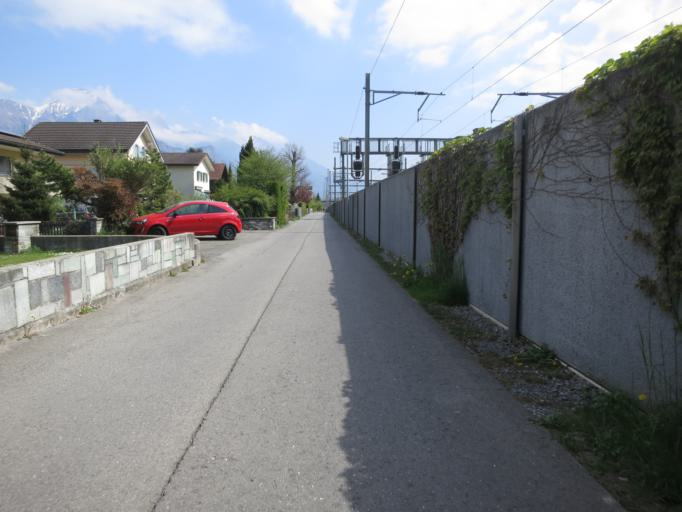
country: CH
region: Saint Gallen
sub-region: Wahlkreis Sarganserland
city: Sargans
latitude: 47.0479
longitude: 9.4361
